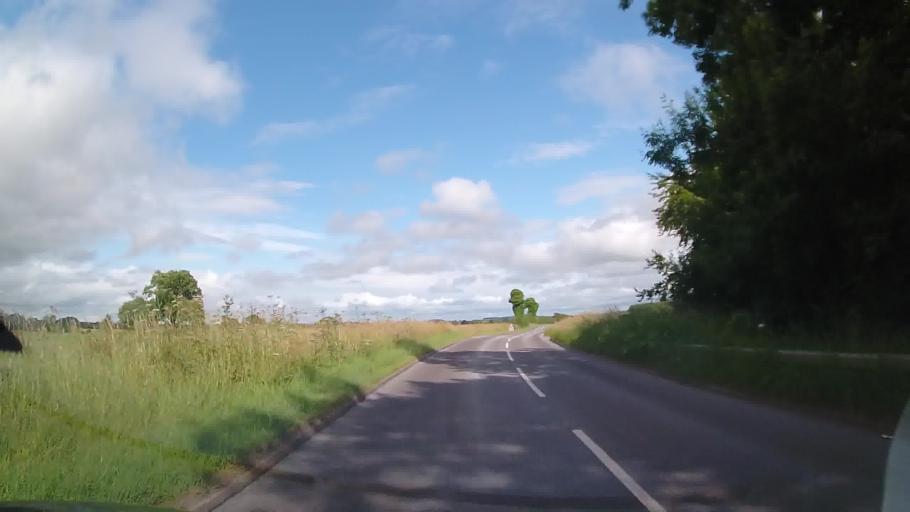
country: GB
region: England
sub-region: Shropshire
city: Pant
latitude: 52.8102
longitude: -3.0384
